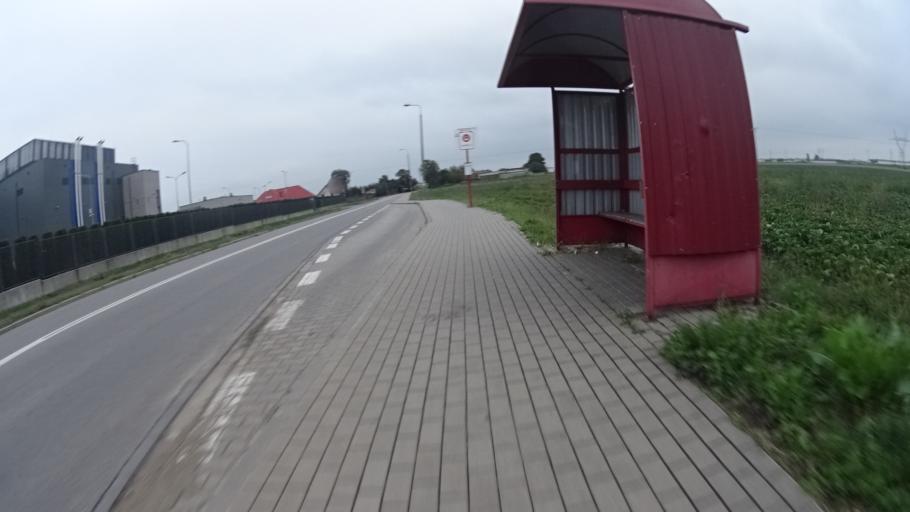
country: PL
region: Masovian Voivodeship
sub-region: Powiat warszawski zachodni
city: Babice
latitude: 52.2302
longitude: 20.8347
